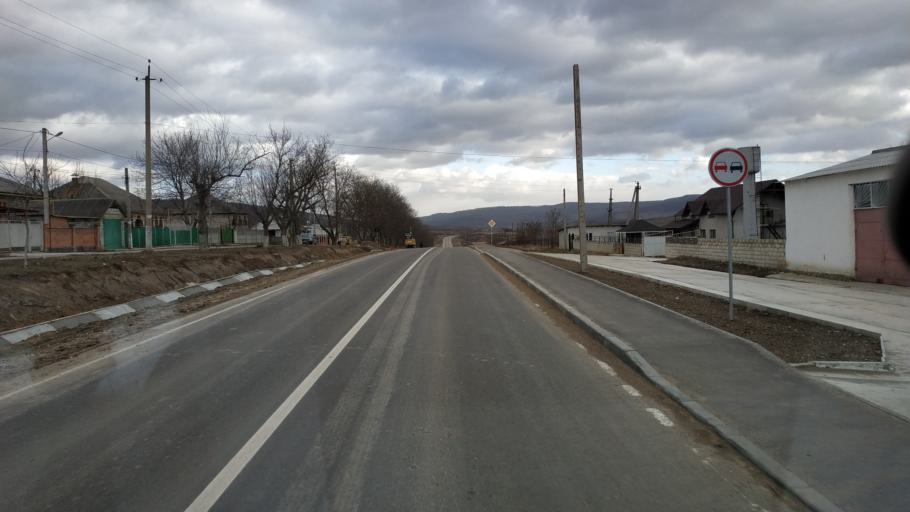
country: MD
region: Calarasi
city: Calarasi
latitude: 47.2763
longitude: 28.2156
